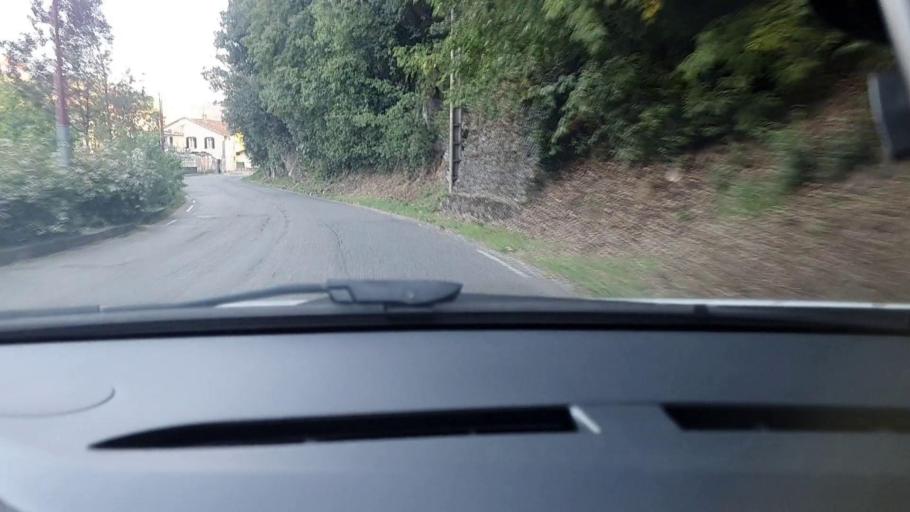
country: FR
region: Languedoc-Roussillon
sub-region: Departement du Gard
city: Besseges
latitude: 44.2963
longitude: 4.0938
